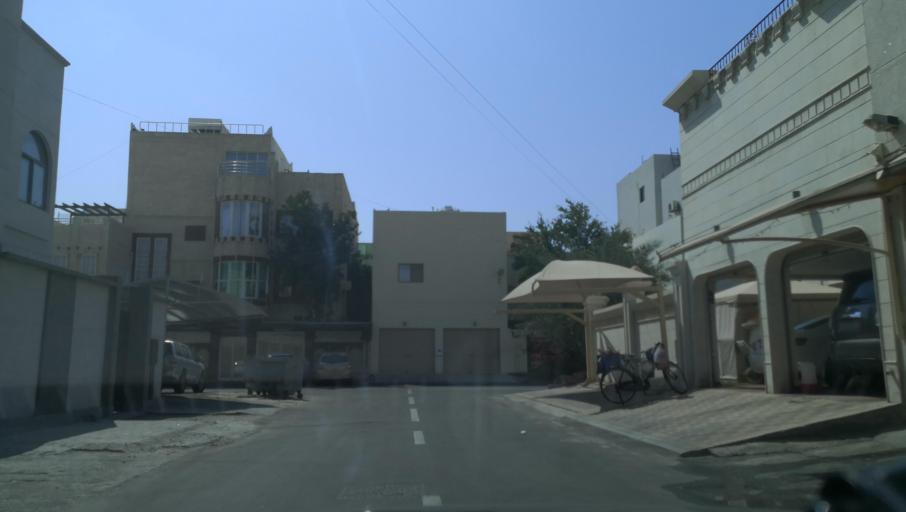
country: BH
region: Muharraq
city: Al Hadd
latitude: 26.2519
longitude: 50.6472
